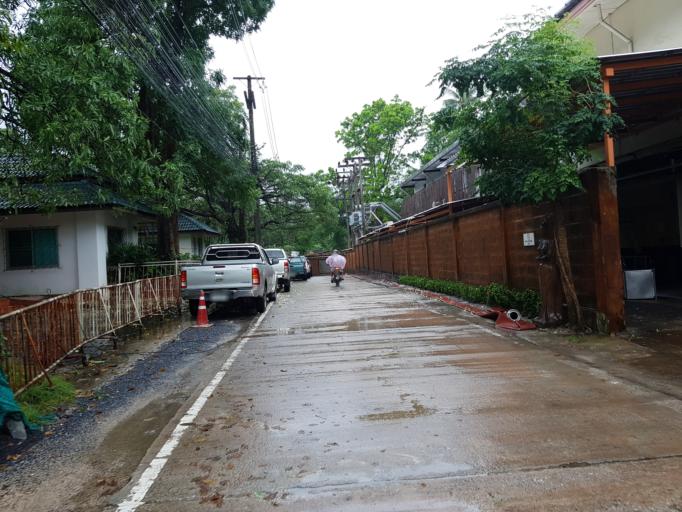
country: TH
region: Surat Thani
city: Ko Samui
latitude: 9.5609
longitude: 100.0253
